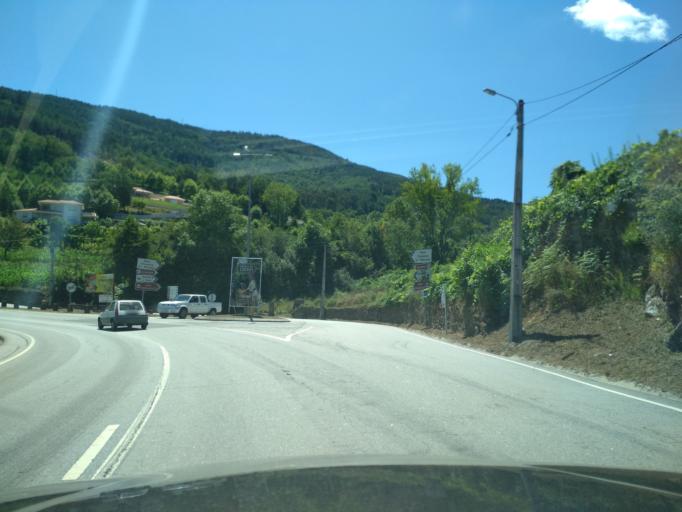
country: PT
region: Vila Real
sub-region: Ribeira de Pena
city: Sobreira
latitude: 41.5232
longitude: -7.7875
